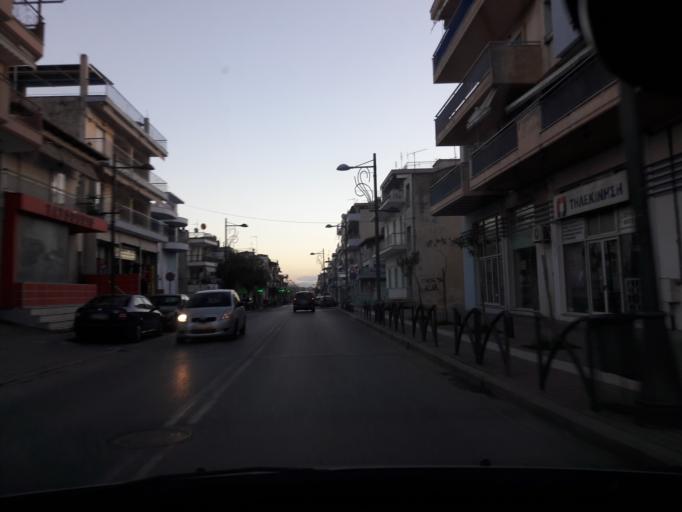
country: GR
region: Central Macedonia
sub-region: Nomos Thessalonikis
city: Stavroupoli
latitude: 40.6710
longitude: 22.9335
